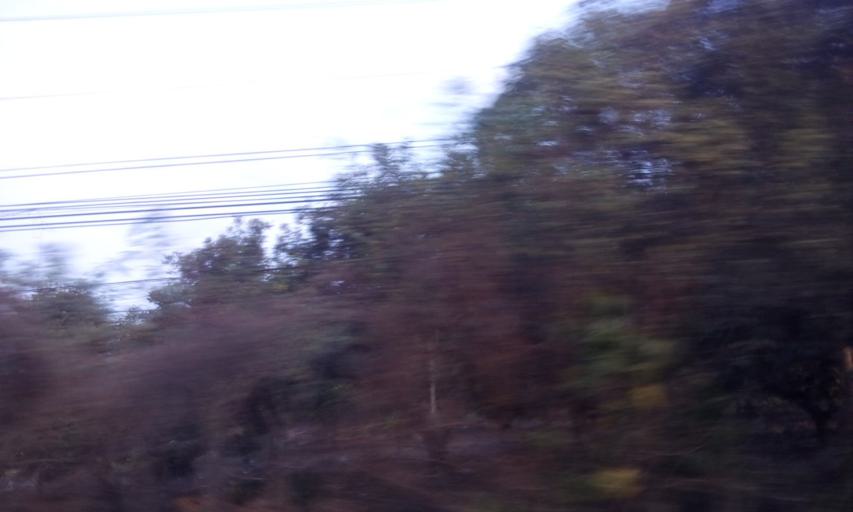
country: TH
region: Trat
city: Khao Saming
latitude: 12.3603
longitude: 102.3836
